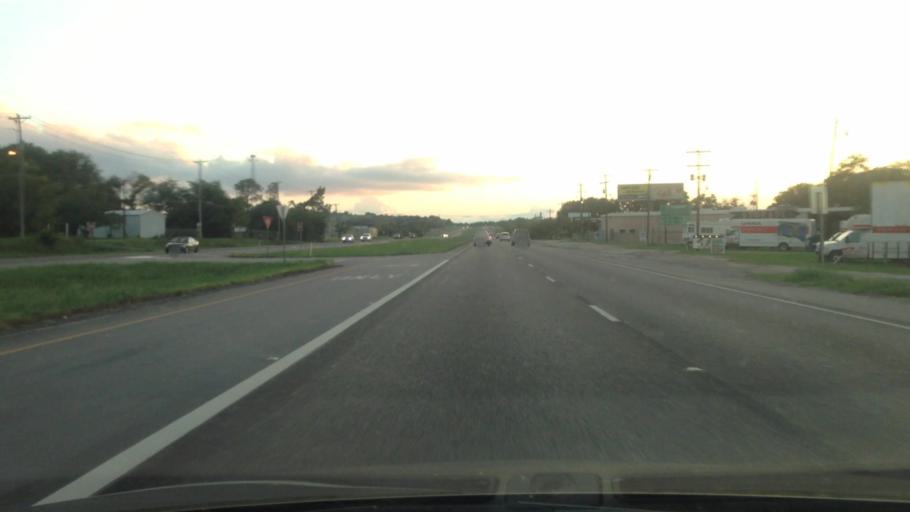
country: US
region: Texas
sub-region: Tarrant County
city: Benbrook
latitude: 32.6169
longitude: -97.5377
